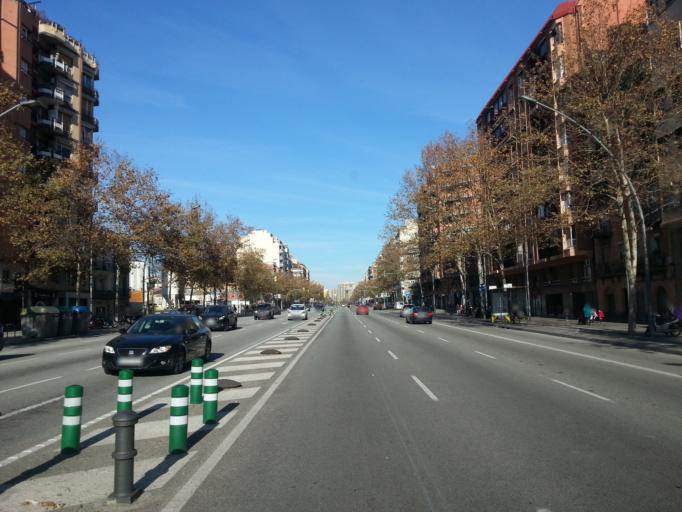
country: ES
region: Catalonia
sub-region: Provincia de Barcelona
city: Sant Marti
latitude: 41.4124
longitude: 2.1870
